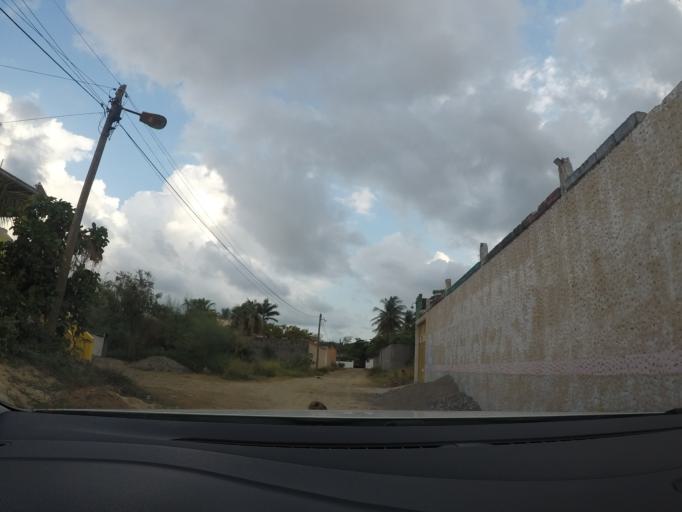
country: MX
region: Oaxaca
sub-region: Salina Cruz
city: Salina Cruz
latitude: 16.2113
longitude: -95.1961
